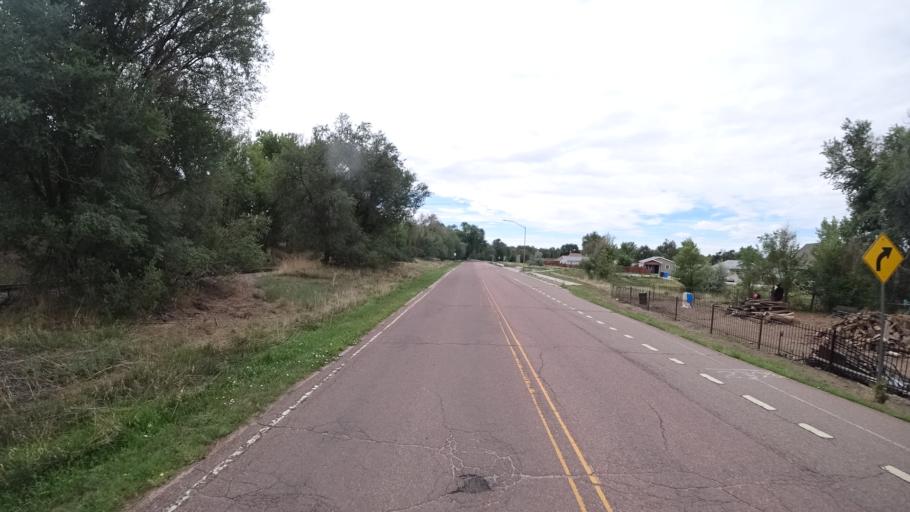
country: US
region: Colorado
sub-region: El Paso County
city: Fountain
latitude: 38.6918
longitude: -104.7021
